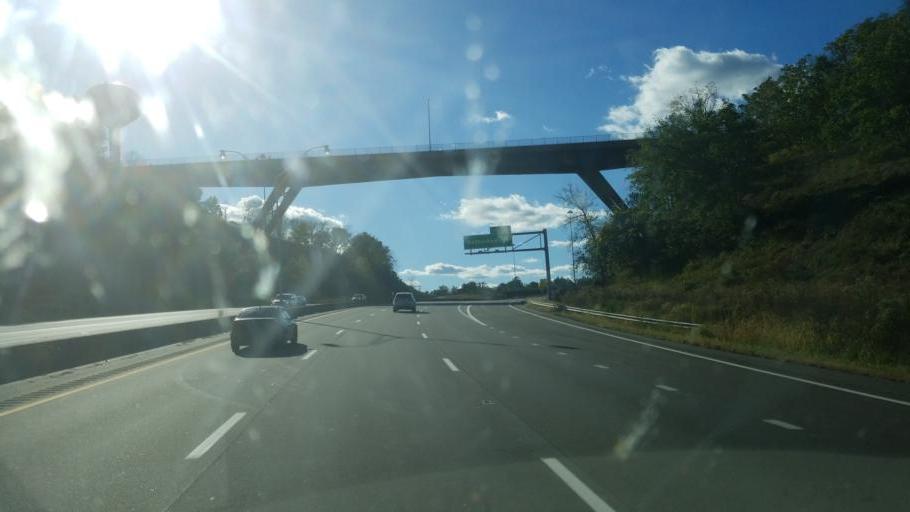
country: US
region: West Virginia
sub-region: Ohio County
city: Bethlehem
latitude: 40.0488
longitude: -80.6902
